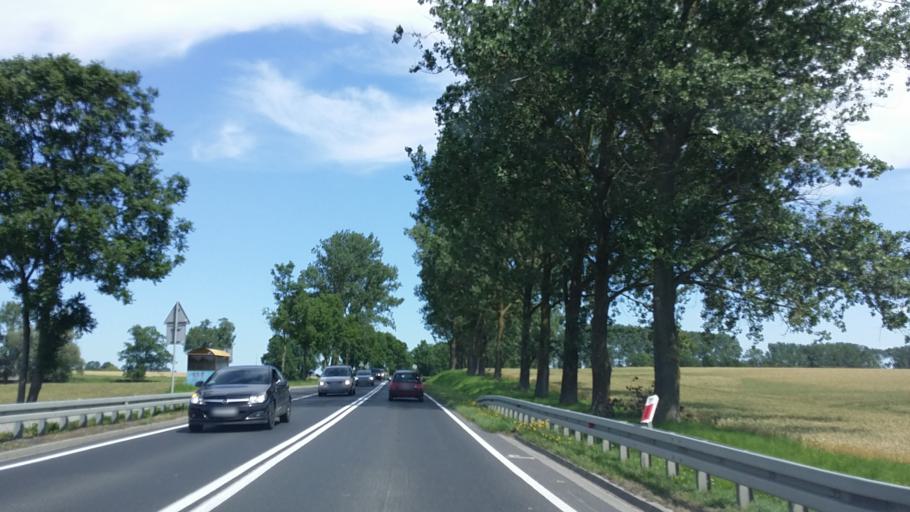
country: PL
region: West Pomeranian Voivodeship
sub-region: Powiat koszalinski
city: Mielno
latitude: 54.2232
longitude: 16.0282
